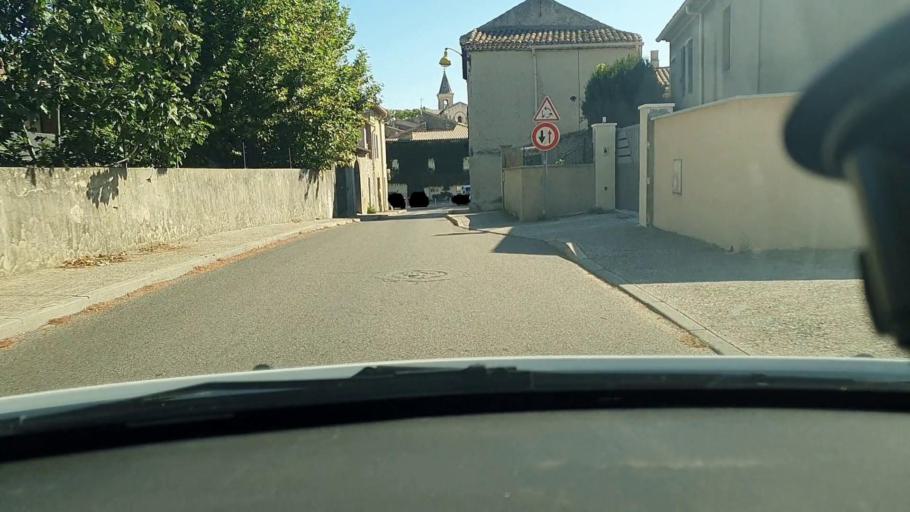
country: FR
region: Languedoc-Roussillon
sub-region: Departement du Gard
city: Saint-Paulet-de-Caisson
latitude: 44.2634
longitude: 4.5958
